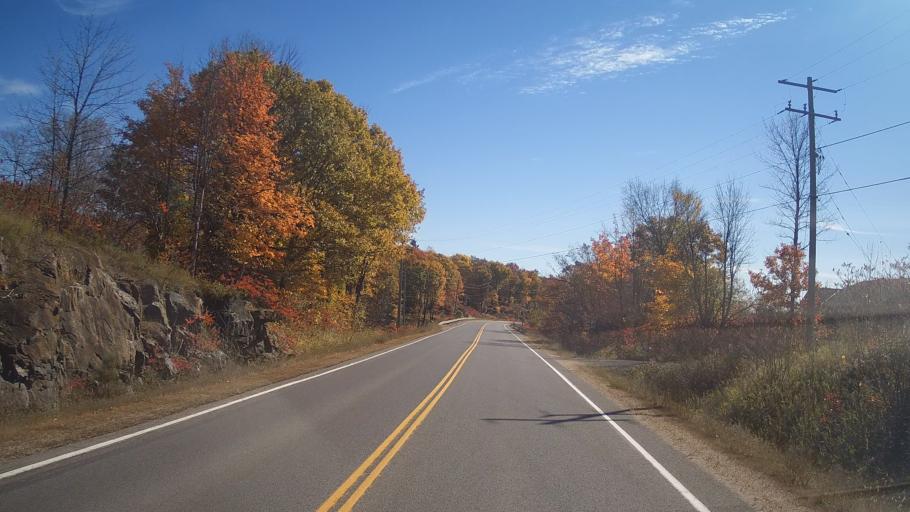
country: CA
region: Ontario
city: Perth
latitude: 44.6781
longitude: -76.6715
